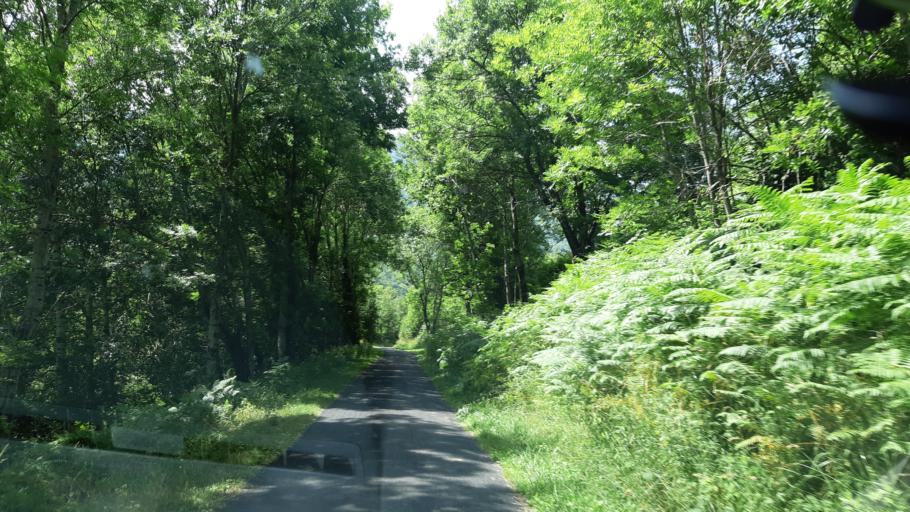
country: FR
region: Languedoc-Roussillon
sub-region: Departement des Pyrenees-Orientales
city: Vinca
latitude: 42.5345
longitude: 2.5216
